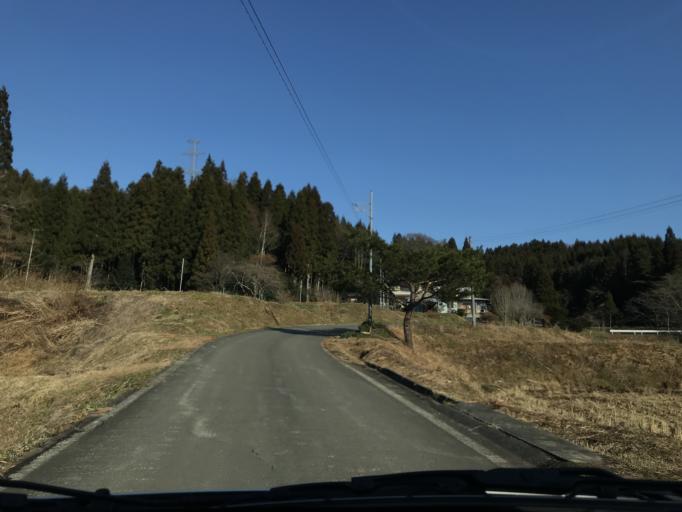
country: JP
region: Iwate
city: Ichinoseki
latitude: 38.9735
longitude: 141.0388
